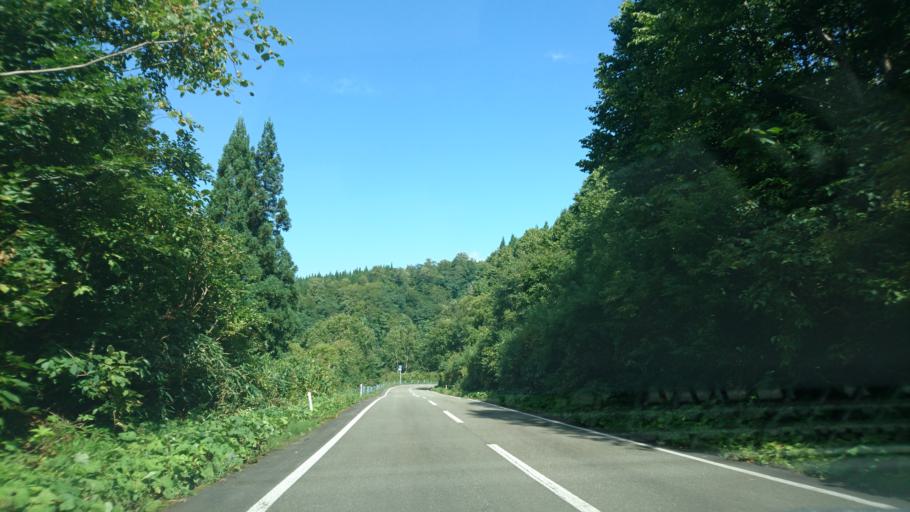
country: JP
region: Akita
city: Yuzawa
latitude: 38.9645
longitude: 140.7140
